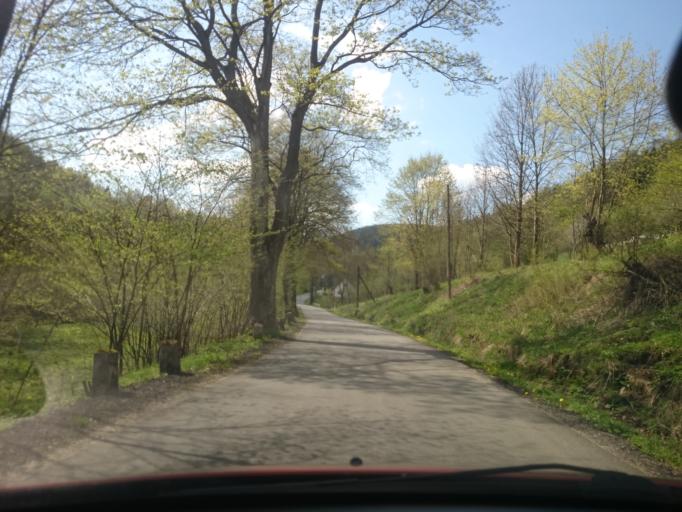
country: PL
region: Lower Silesian Voivodeship
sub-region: Powiat klodzki
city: Bystrzyca Klodzka
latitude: 50.3011
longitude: 16.5411
